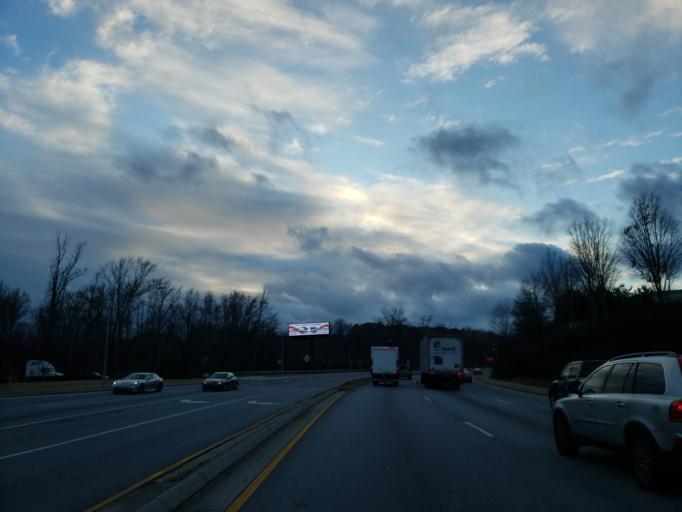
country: US
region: Georgia
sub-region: Fulton County
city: College Park
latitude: 33.6546
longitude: -84.5045
